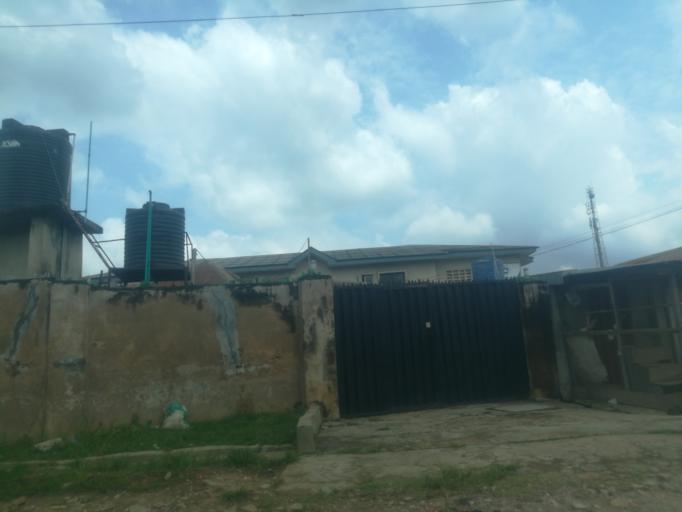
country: NG
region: Oyo
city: Ibadan
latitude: 7.3611
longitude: 3.8445
